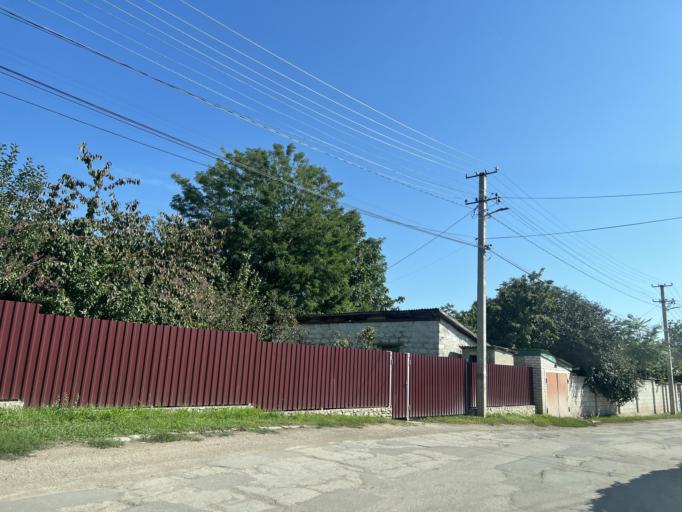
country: MD
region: Ungheni
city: Ungheni
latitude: 47.2005
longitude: 27.7985
